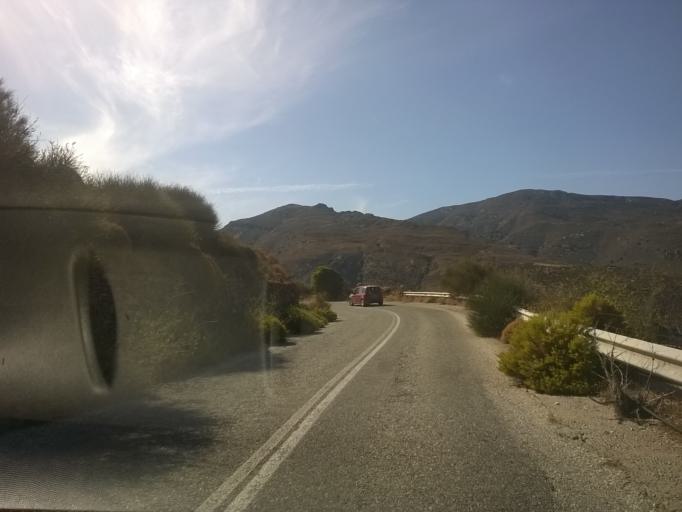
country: GR
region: South Aegean
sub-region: Nomos Kykladon
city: Filotion
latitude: 37.1559
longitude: 25.5522
